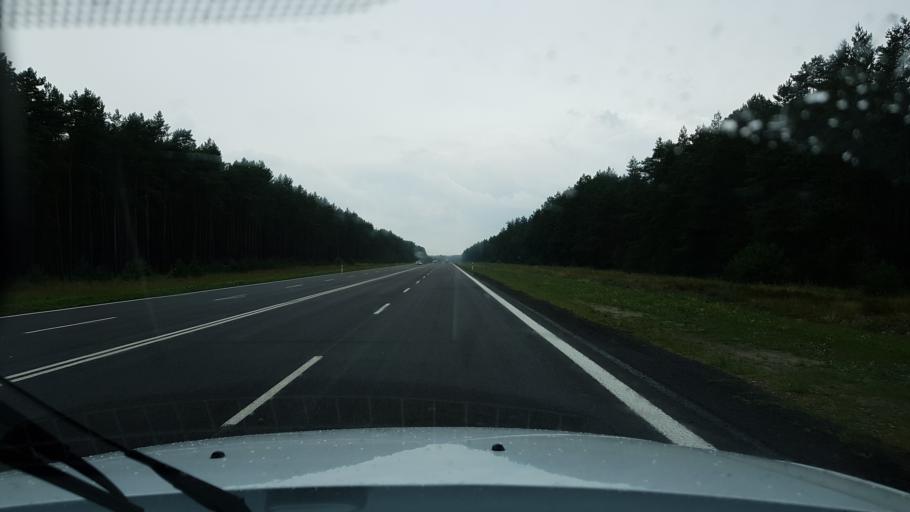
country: PL
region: West Pomeranian Voivodeship
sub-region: Powiat stargardzki
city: Kobylanka
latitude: 53.4278
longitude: 14.8123
